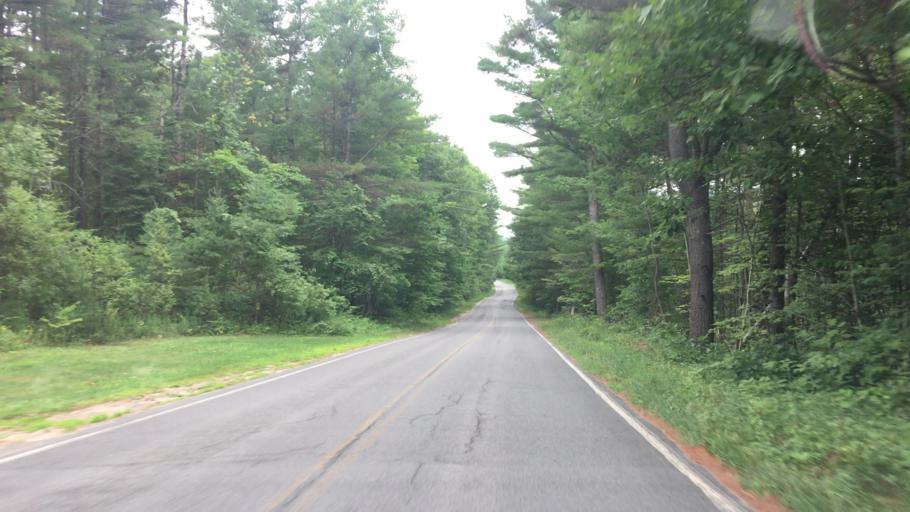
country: US
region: New York
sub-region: Essex County
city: Keeseville
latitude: 44.4354
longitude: -73.6217
